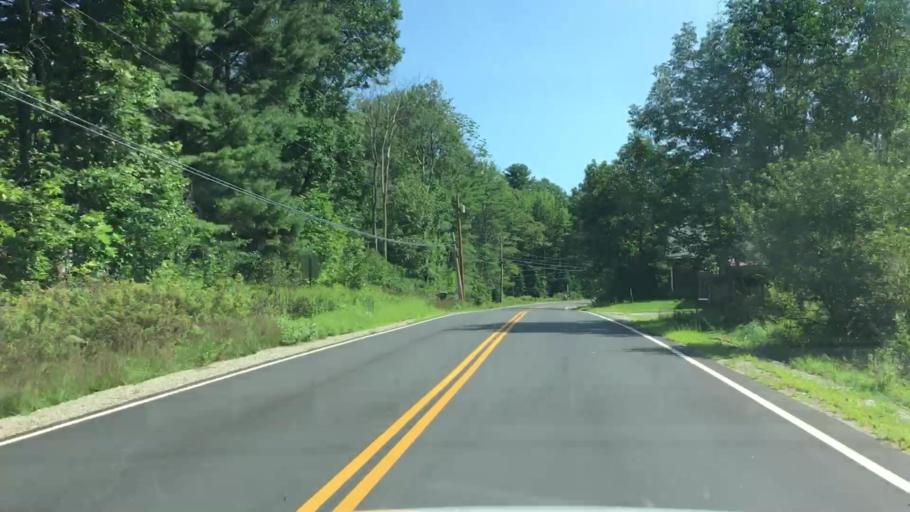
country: US
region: Maine
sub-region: Sagadahoc County
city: Topsham
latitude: 44.0176
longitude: -69.9292
